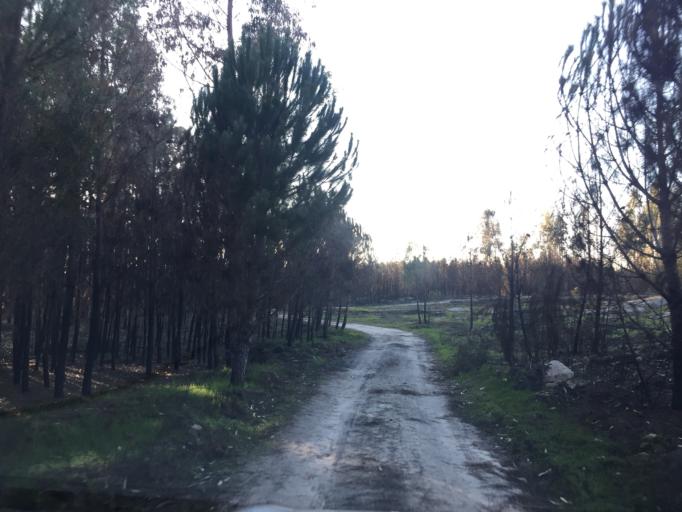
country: PT
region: Viseu
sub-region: Concelho de Carregal do Sal
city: Carregal do Sal
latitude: 40.4633
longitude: -7.9249
